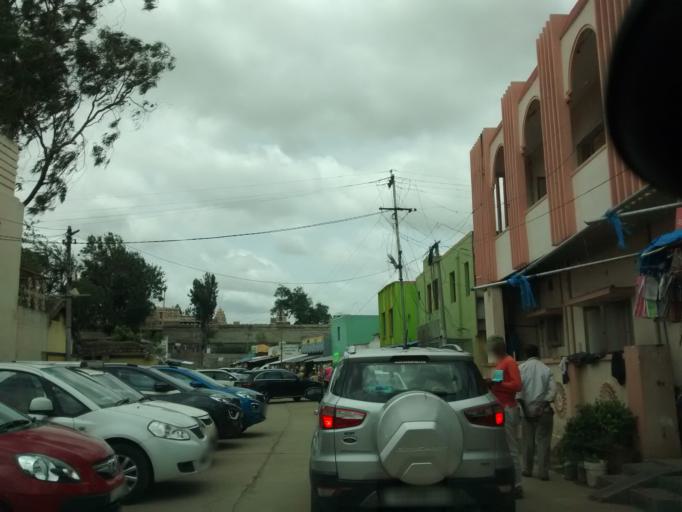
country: IN
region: Andhra Pradesh
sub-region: Anantapur
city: Hindupur
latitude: 13.8034
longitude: 77.6091
